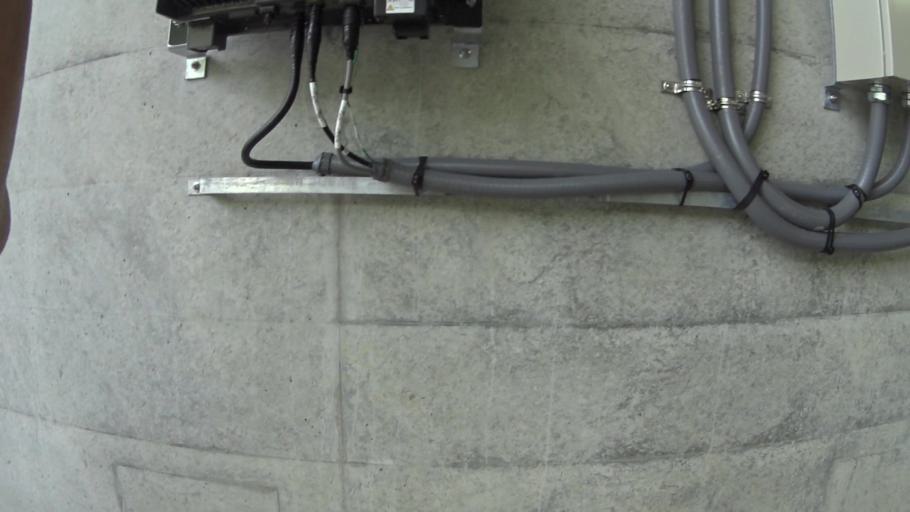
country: JP
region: Kyoto
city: Ayabe
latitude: 35.1615
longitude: 135.3978
